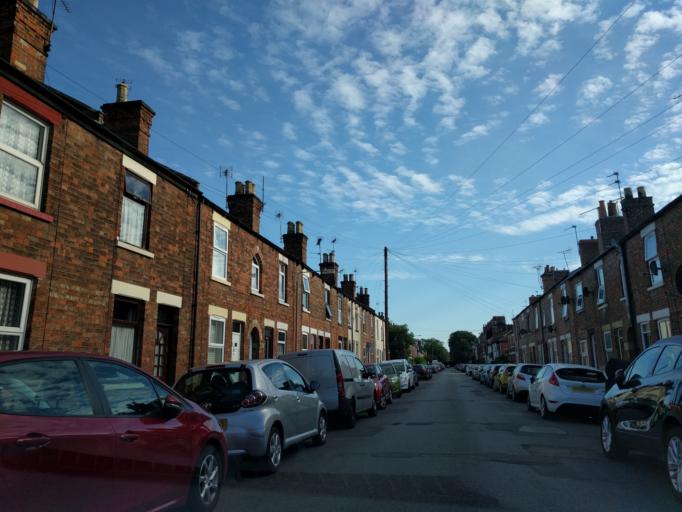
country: GB
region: England
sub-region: Nottinghamshire
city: Newark on Trent
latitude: 53.0729
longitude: -0.7986
